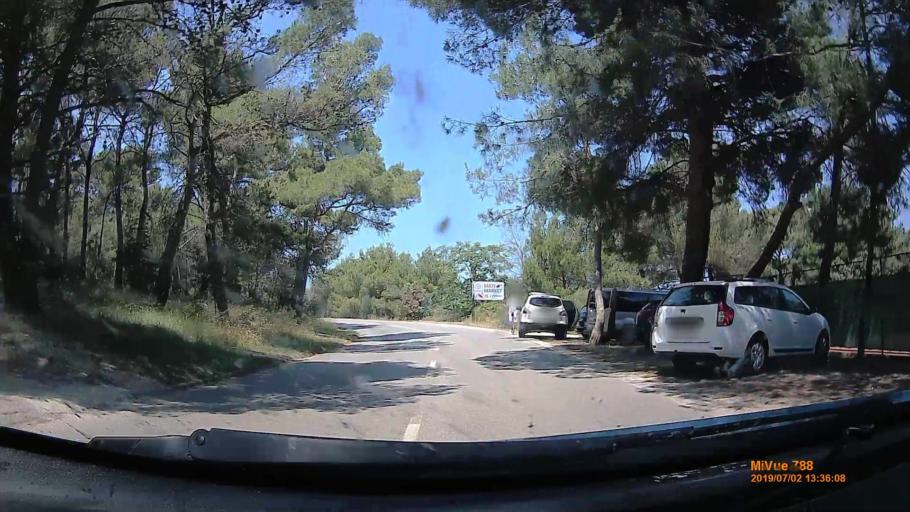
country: HR
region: Primorsko-Goranska
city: Mali Losinj
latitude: 44.5215
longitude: 14.4974
